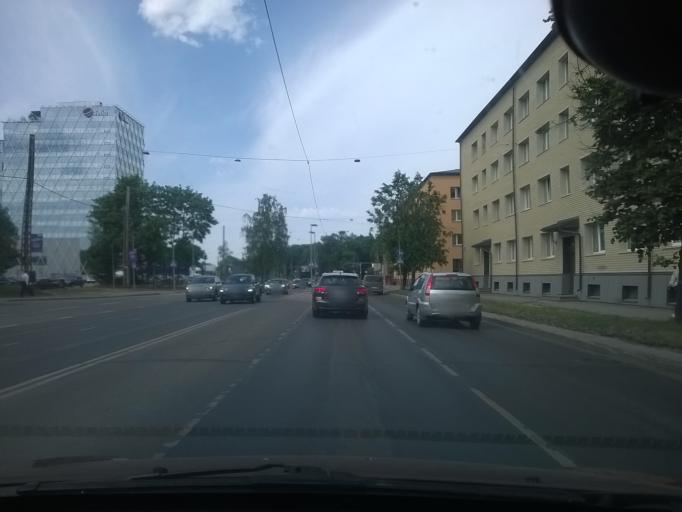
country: EE
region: Harju
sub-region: Tallinna linn
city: Tallinn
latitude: 59.4285
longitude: 24.7092
